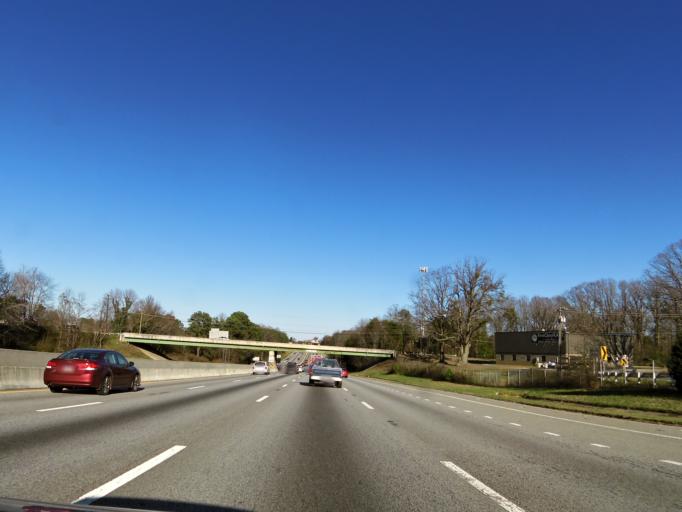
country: US
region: South Carolina
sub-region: Greenville County
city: Mauldin
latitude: 34.8373
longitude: -82.2903
